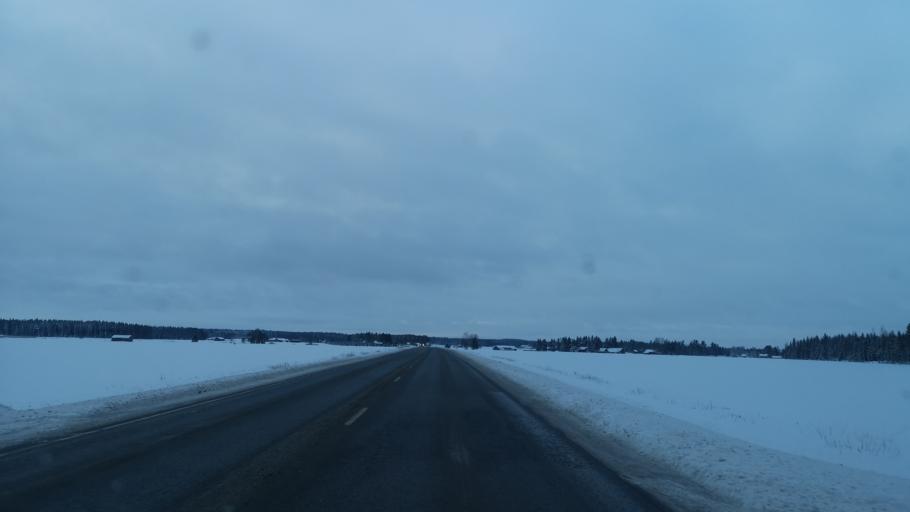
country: FI
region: Varsinais-Suomi
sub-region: Loimaa
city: Loimaa
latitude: 60.8921
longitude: 23.1093
